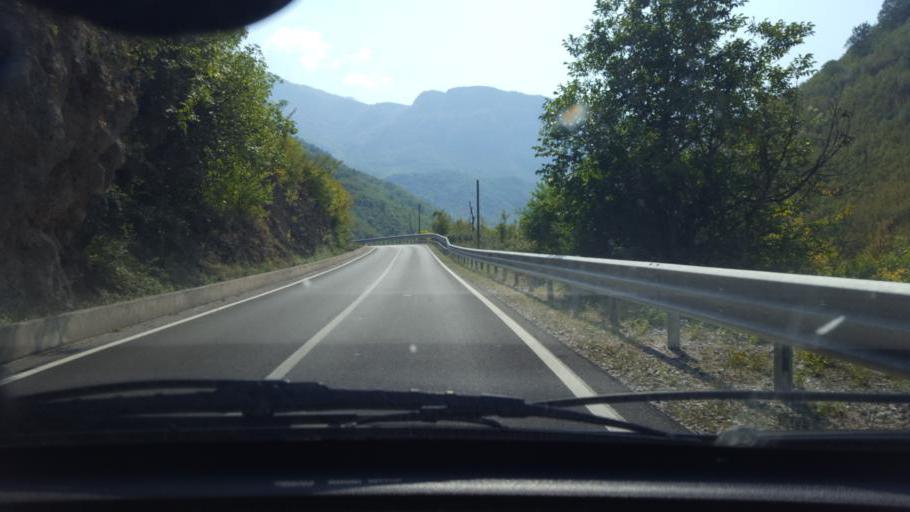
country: AL
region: Shkoder
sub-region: Rrethi i Malesia e Madhe
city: Kastrat
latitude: 42.4406
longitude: 19.5385
